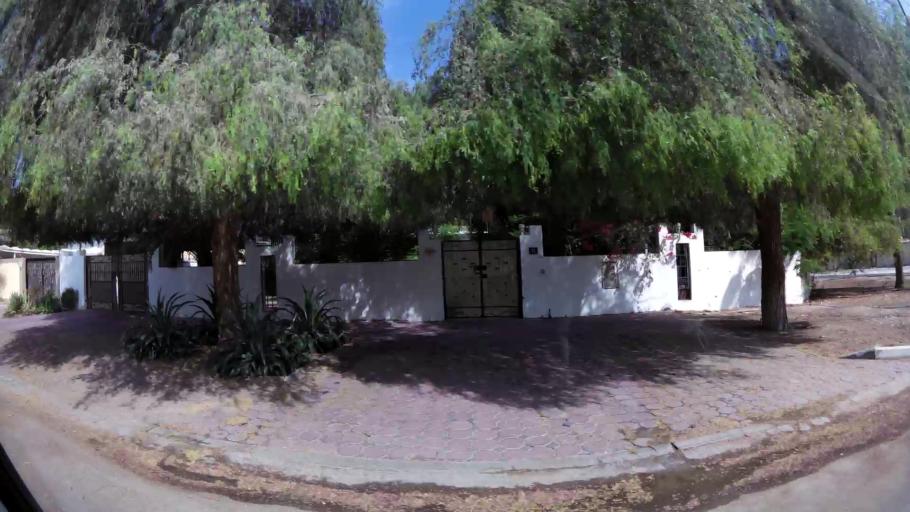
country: AE
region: Ash Shariqah
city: Sharjah
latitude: 25.2707
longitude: 55.4020
